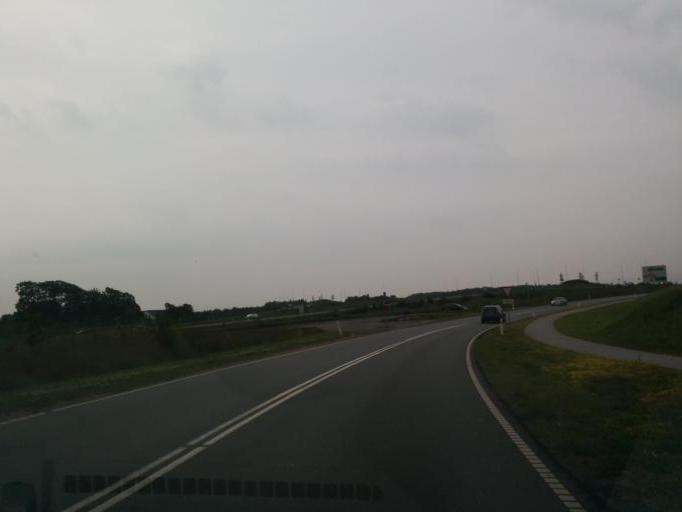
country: DK
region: Central Jutland
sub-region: Arhus Kommune
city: Logten
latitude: 56.2516
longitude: 10.3023
